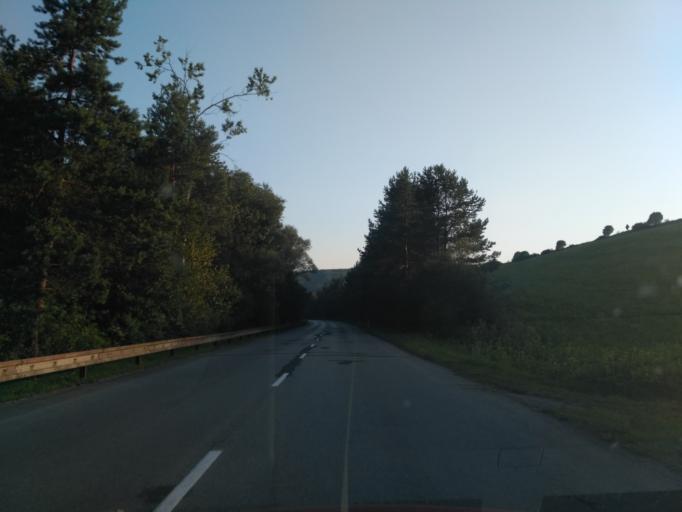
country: SK
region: Presovsky
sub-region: Okres Presov
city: Presov
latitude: 48.9618
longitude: 21.1652
